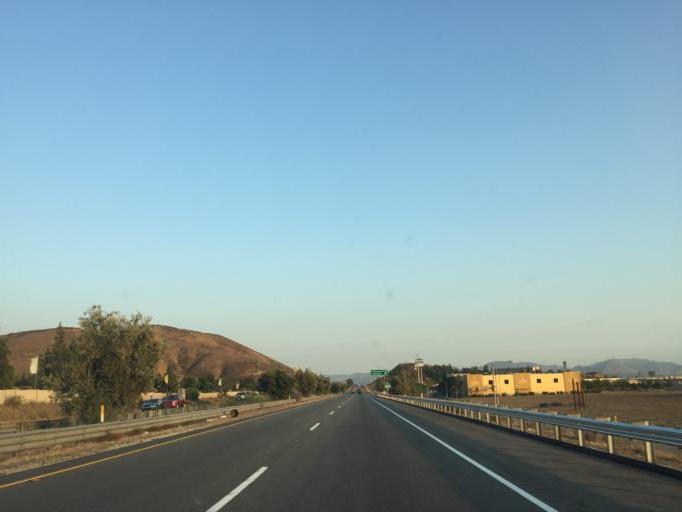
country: US
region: California
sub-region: San Bernardino County
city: Muscoy
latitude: 34.1693
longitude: -117.3377
